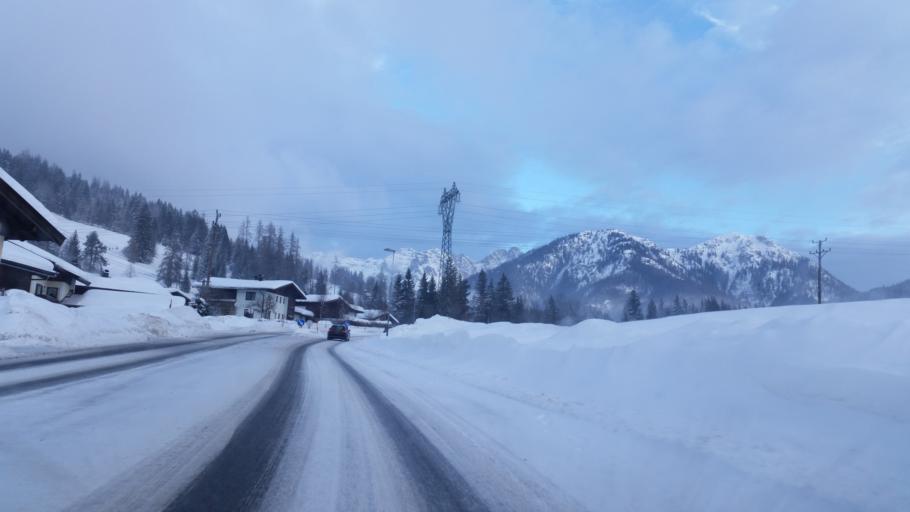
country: AT
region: Tyrol
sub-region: Politischer Bezirk Kitzbuhel
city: Hochfilzen
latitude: 47.4661
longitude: 12.6058
